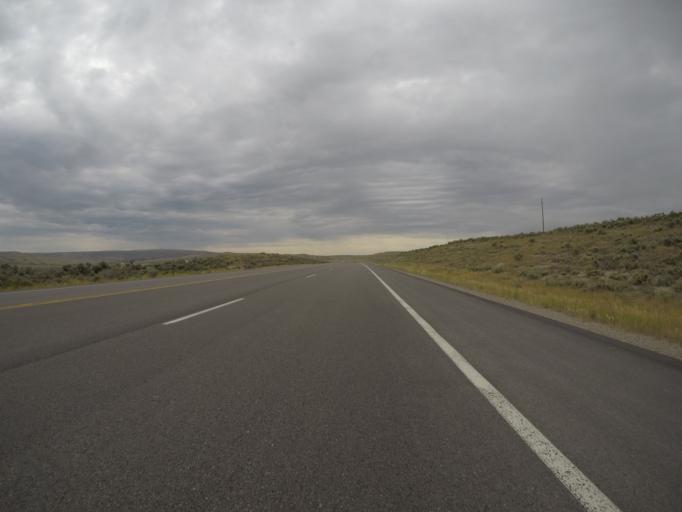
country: US
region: Wyoming
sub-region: Lincoln County
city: Kemmerer
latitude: 41.8028
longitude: -110.6012
